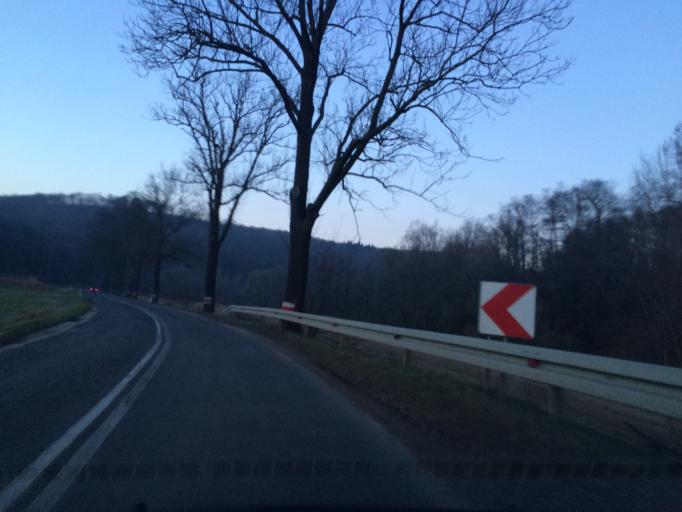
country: PL
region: Lower Silesian Voivodeship
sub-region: Powiat zlotoryjski
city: Zlotoryja
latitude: 51.1172
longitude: 15.8899
